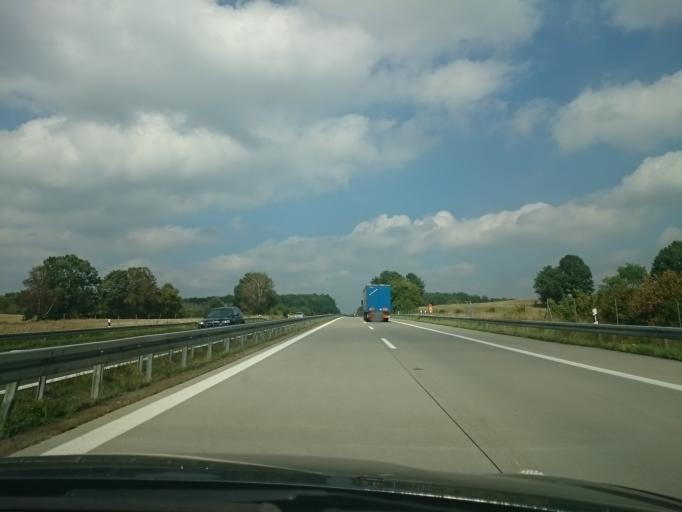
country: DE
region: Brandenburg
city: Althuttendorf
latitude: 52.9824
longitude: 13.8197
